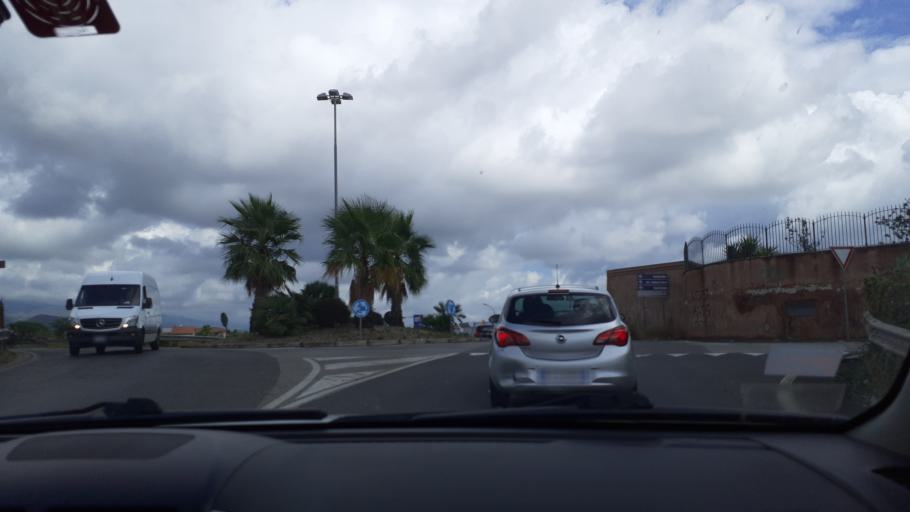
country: IT
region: Sicily
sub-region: Catania
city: San Giovanni la Punta
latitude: 37.5749
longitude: 15.1031
